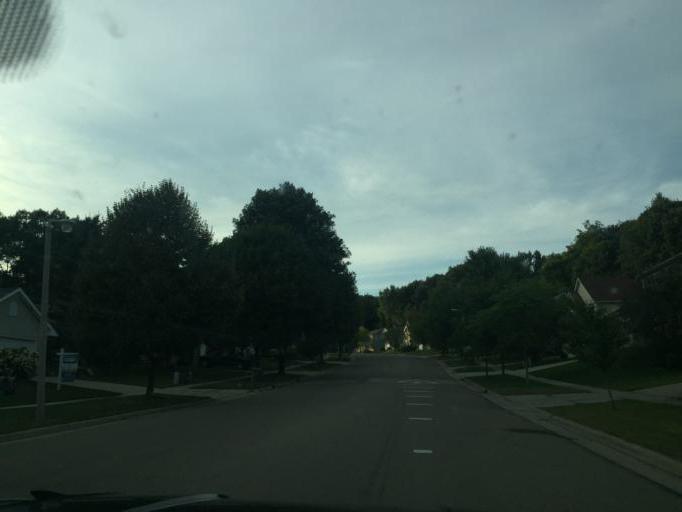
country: US
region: Minnesota
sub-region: Olmsted County
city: Rochester
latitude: 44.0085
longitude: -92.4925
